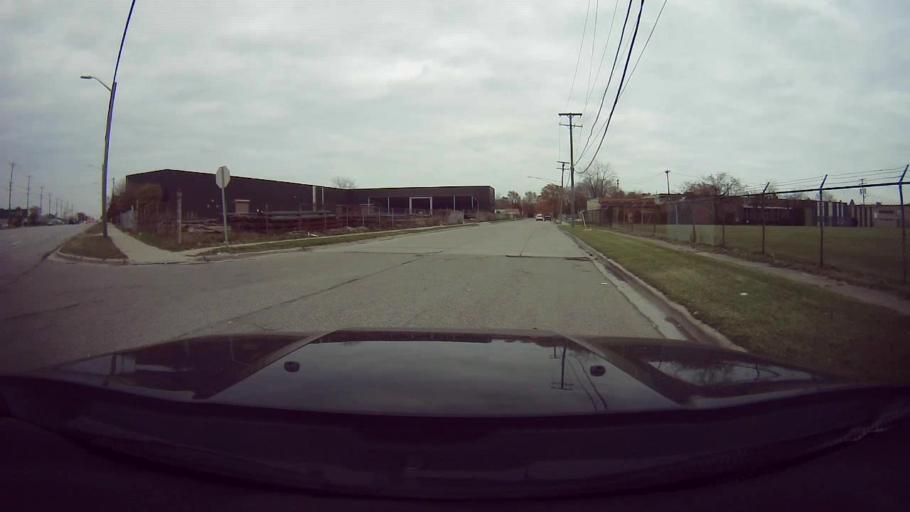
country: US
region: Michigan
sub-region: Macomb County
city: Warren
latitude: 42.4608
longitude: -82.9937
